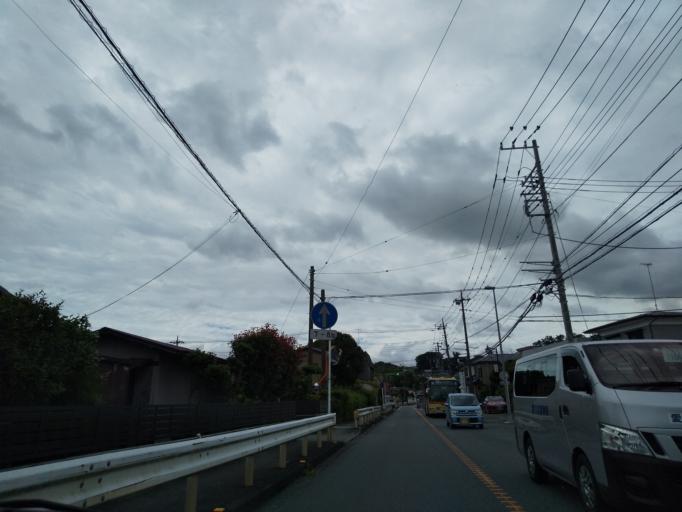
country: JP
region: Kanagawa
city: Zama
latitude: 35.5164
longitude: 139.3653
